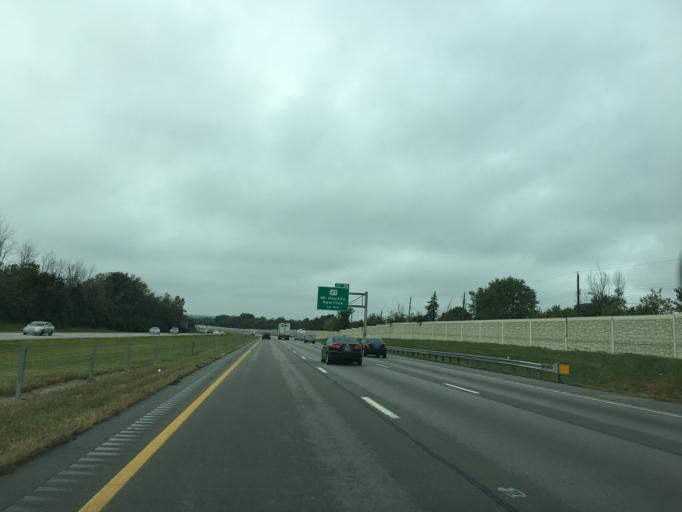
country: US
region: Ohio
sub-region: Hamilton County
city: Pleasant Run Farm
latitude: 39.2940
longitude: -84.5464
